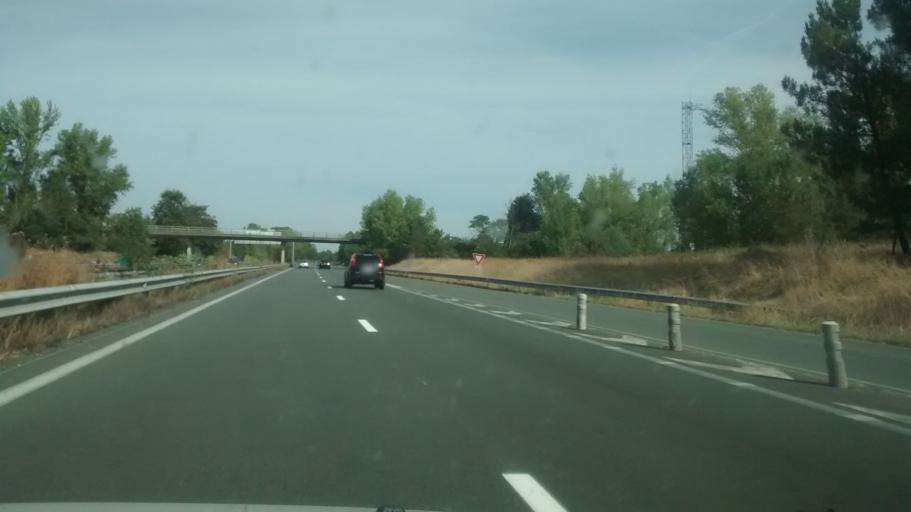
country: FR
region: Aquitaine
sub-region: Departement du Lot-et-Garonne
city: Damazan
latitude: 44.2828
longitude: 0.2681
